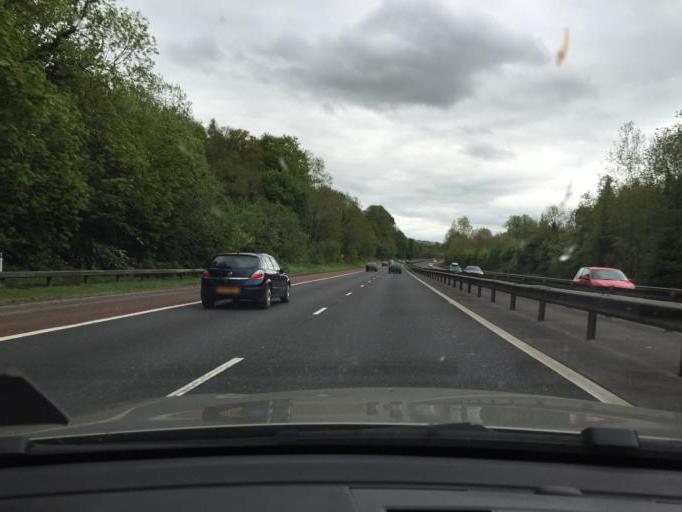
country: GB
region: Northern Ireland
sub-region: Lisburn District
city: Lisburn
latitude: 54.5480
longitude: -5.9953
